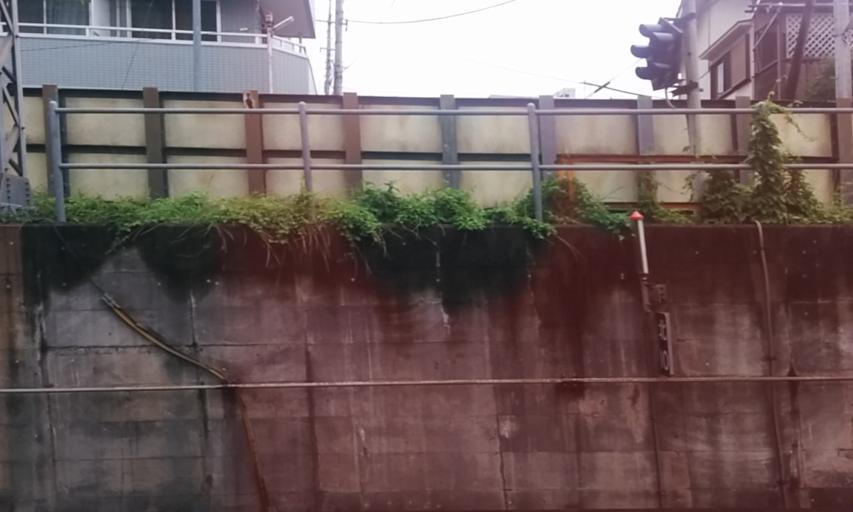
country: JP
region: Tokyo
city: Hachioji
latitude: 35.6561
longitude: 139.3461
